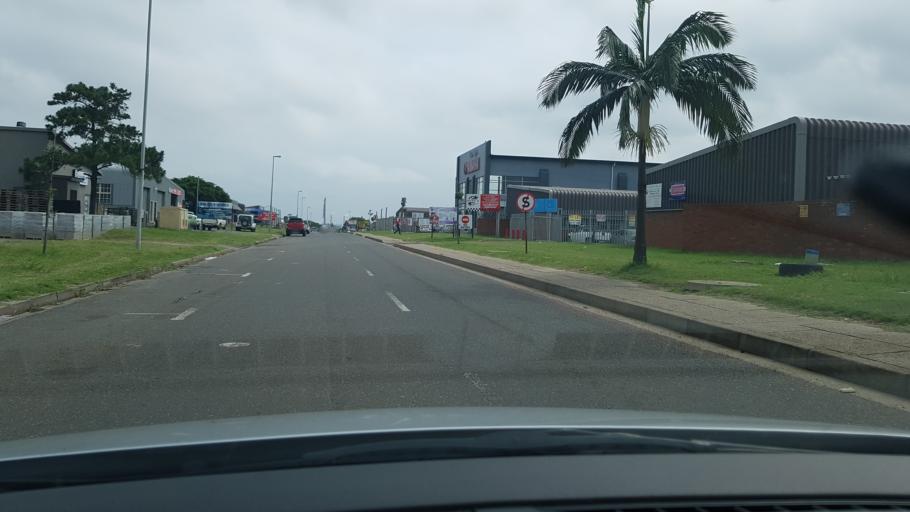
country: ZA
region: KwaZulu-Natal
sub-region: uThungulu District Municipality
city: Richards Bay
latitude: -28.7539
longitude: 32.0444
